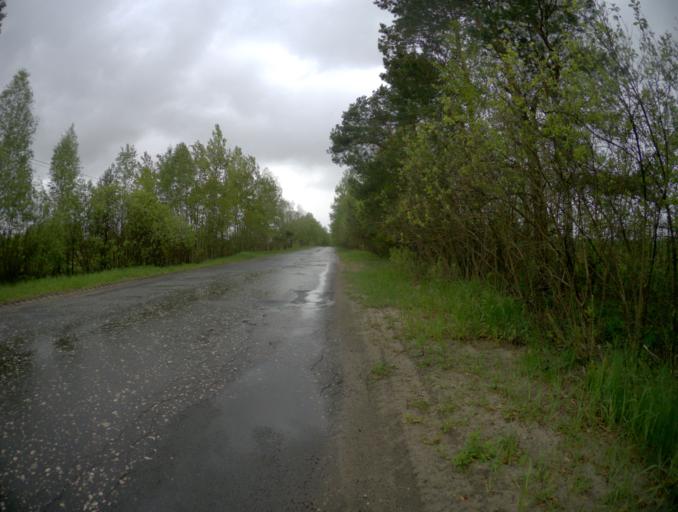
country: RU
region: Vladimir
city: Velikodvorskiy
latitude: 55.3718
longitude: 40.8364
